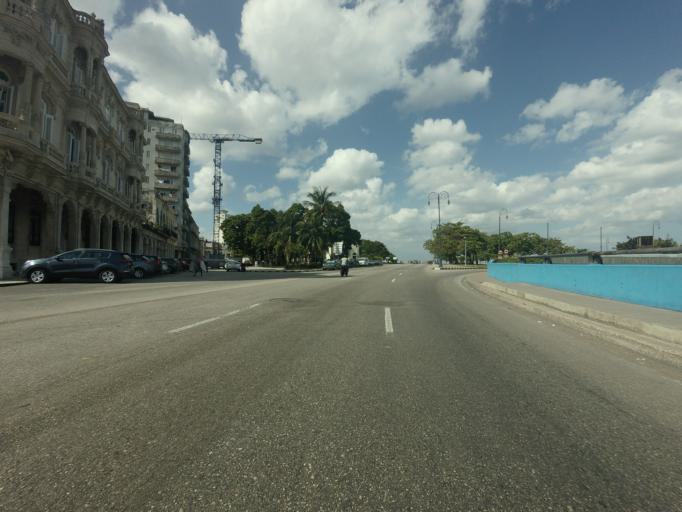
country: CU
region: La Habana
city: Centro Habana
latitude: 23.1439
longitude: -82.3567
